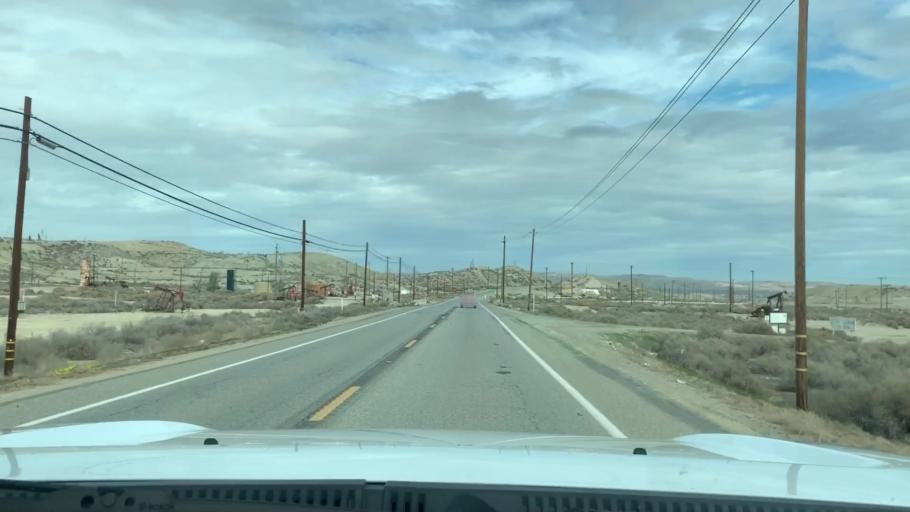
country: US
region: California
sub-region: Kern County
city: Maricopa
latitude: 35.0732
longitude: -119.4020
